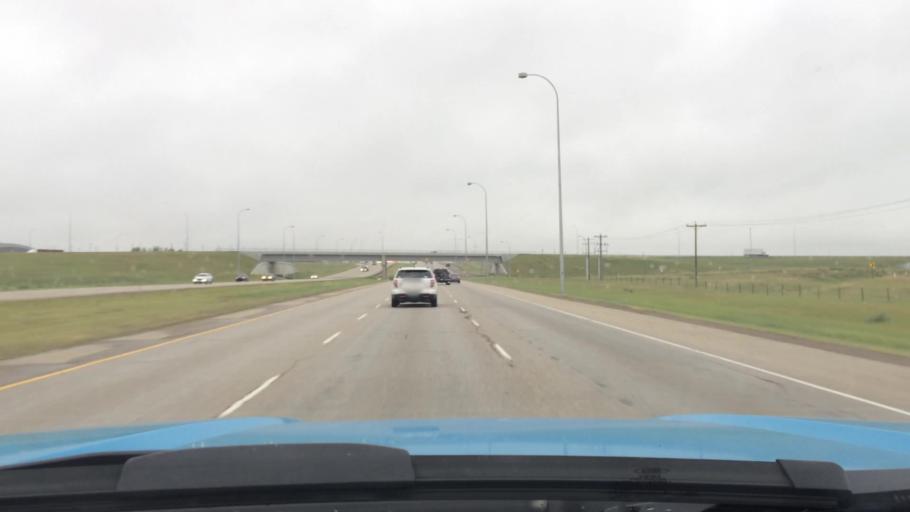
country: CA
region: Alberta
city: Airdrie
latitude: 51.2008
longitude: -114.0017
